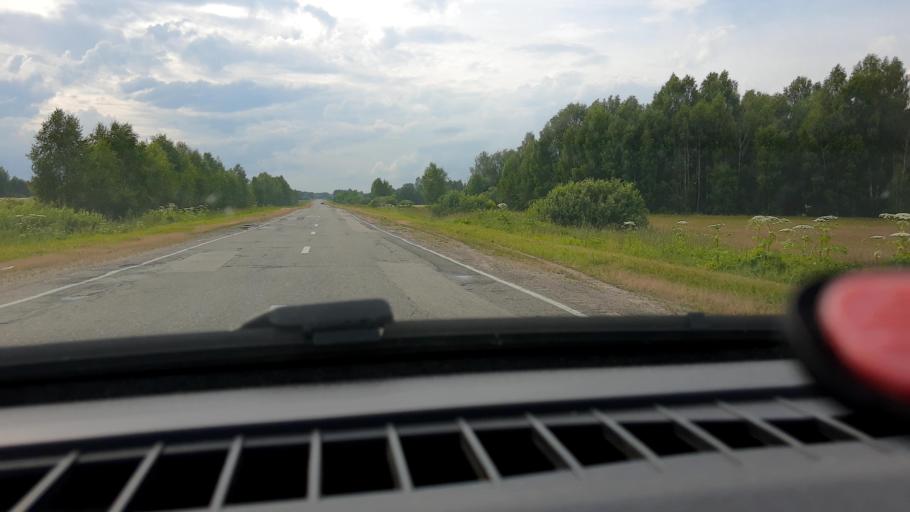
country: RU
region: Nizjnij Novgorod
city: Neklyudovo
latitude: 56.5010
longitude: 43.9896
